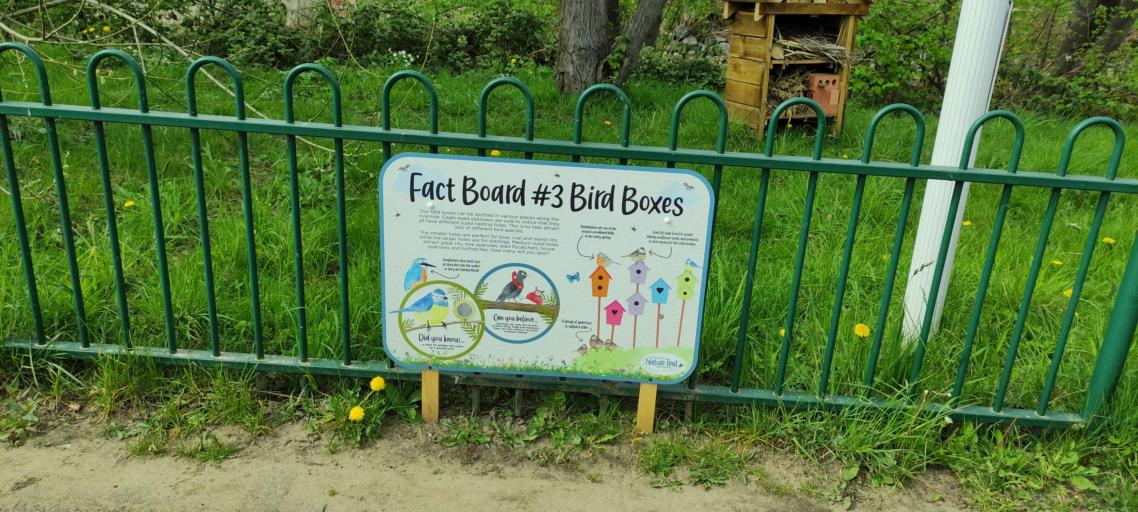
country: GB
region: England
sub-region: Rotherham
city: Wentworth
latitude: 53.4137
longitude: -1.4154
